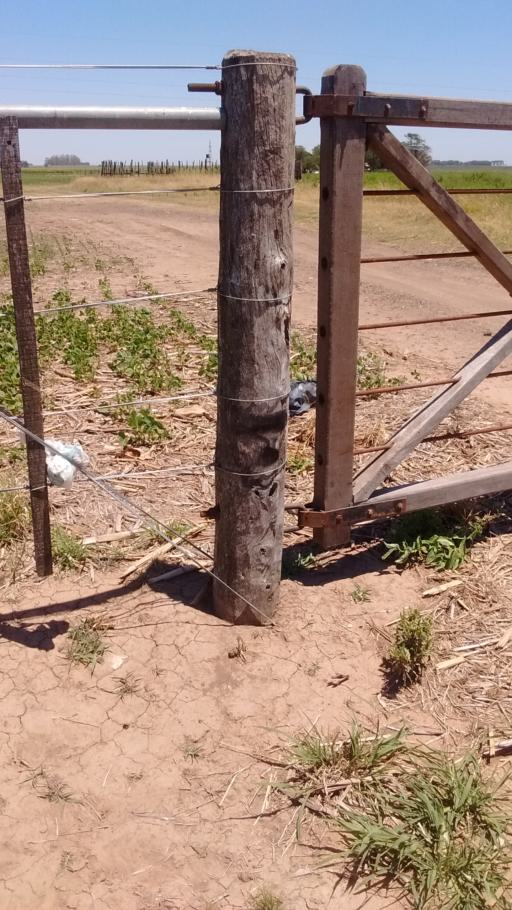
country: AR
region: Santa Fe
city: Las Parejas
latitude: -32.6329
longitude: -61.5458
